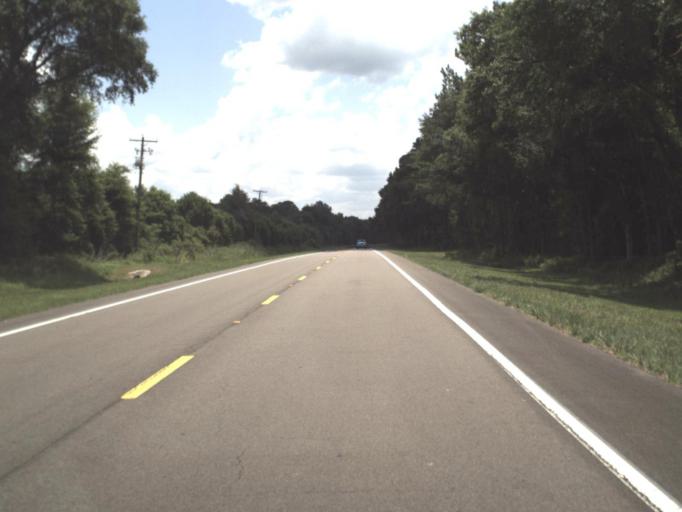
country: US
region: Florida
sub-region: Alachua County
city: Alachua
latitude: 29.8307
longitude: -82.3980
